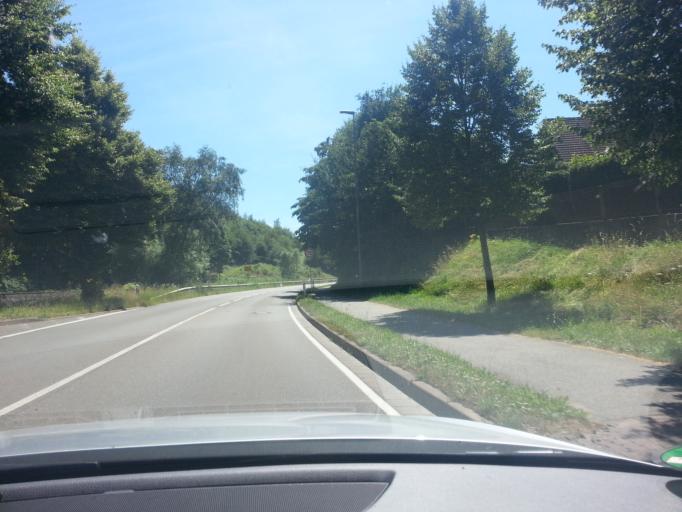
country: DE
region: Rheinland-Pfalz
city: Rammelsbach
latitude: 49.5502
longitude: 7.4531
